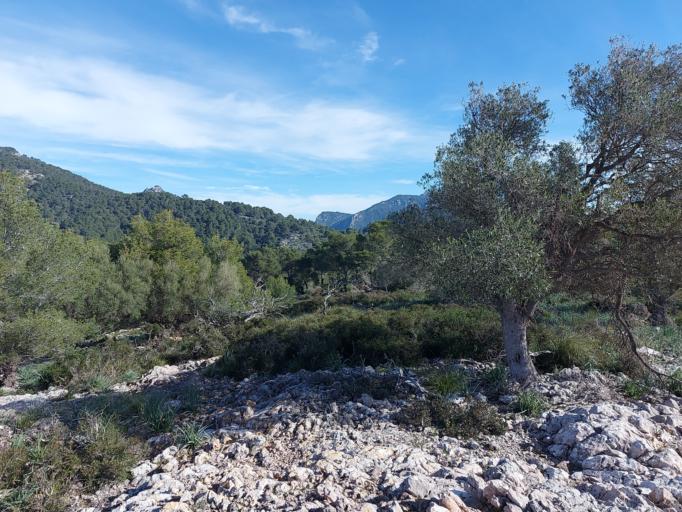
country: ES
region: Balearic Islands
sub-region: Illes Balears
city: Bunyola
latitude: 39.6969
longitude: 2.6639
